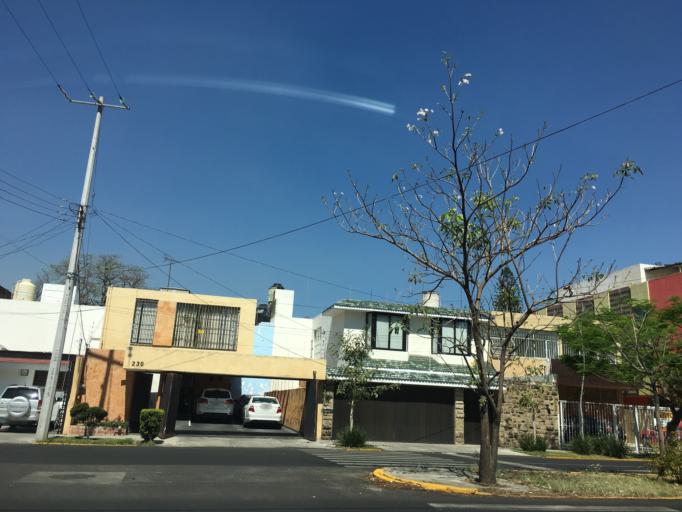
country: MX
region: Jalisco
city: Guadalajara
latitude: 20.6702
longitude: -103.3773
